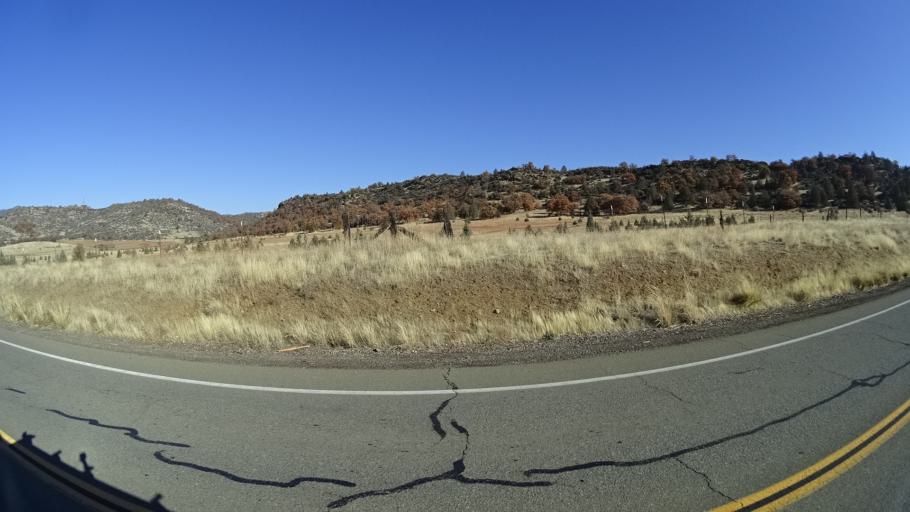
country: US
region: California
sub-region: Siskiyou County
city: Yreka
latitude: 41.7130
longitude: -122.6204
